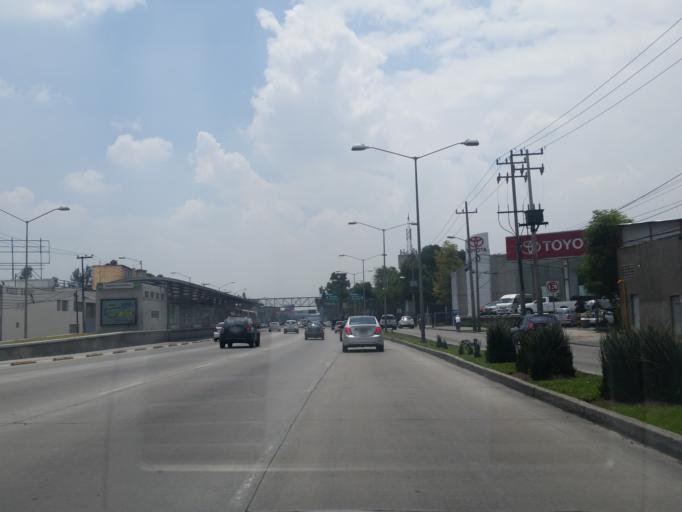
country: MX
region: Mexico
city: Colonia Lindavista
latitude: 19.4847
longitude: -99.1504
